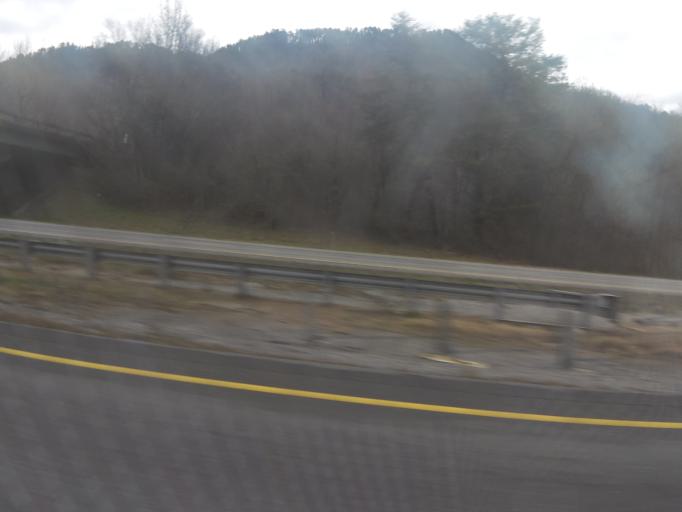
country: US
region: Georgia
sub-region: Dade County
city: Trenton
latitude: 34.9906
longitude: -85.5087
